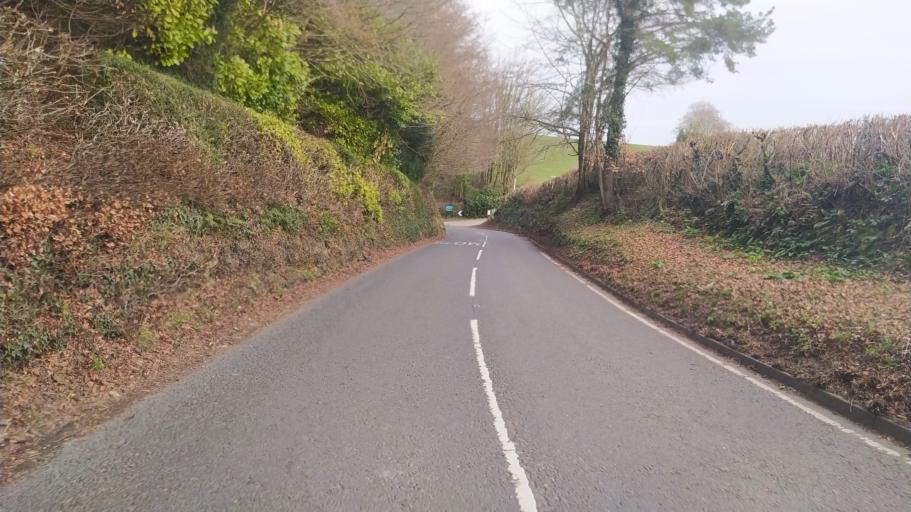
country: GB
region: England
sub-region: Dorset
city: Beaminster
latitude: 50.8515
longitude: -2.7234
